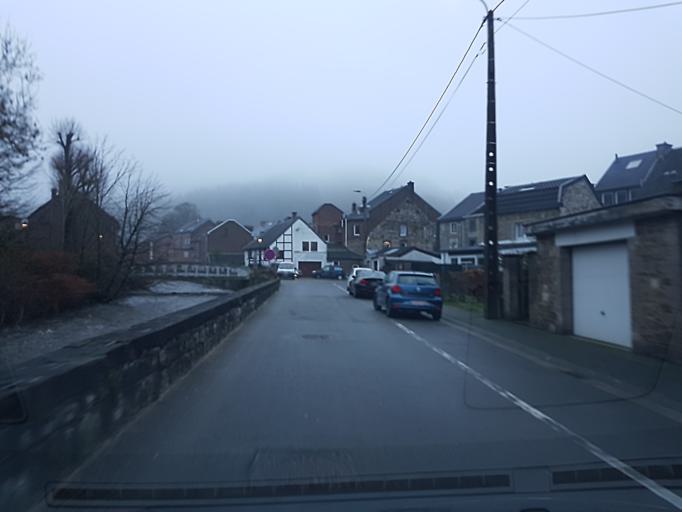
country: BE
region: Wallonia
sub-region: Province de Liege
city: Theux
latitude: 50.5327
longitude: 5.8159
